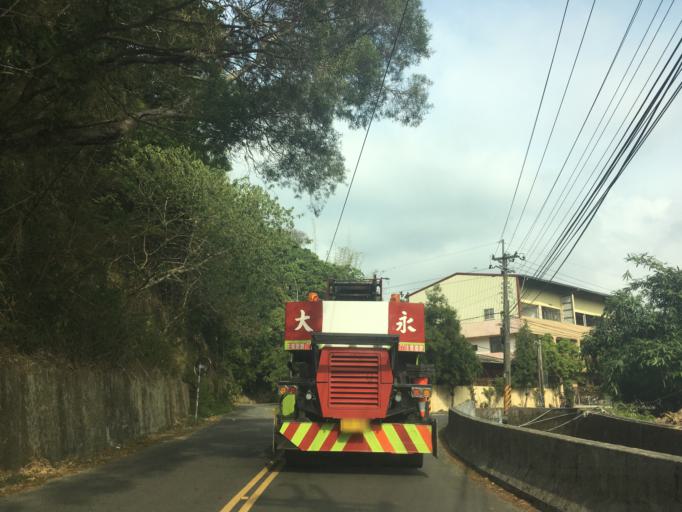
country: TW
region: Taiwan
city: Fengyuan
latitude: 24.2338
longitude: 120.7471
